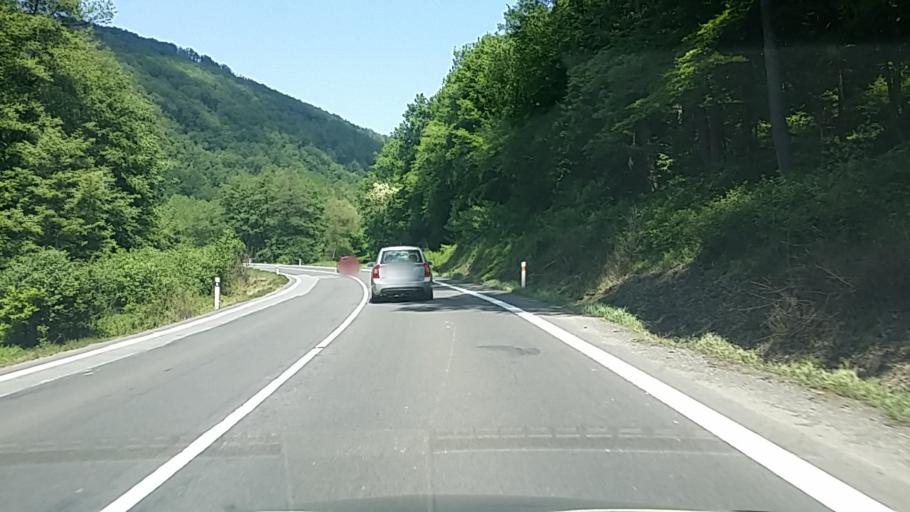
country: SK
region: Banskobystricky
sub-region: Okres Banska Bystrica
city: Zvolen
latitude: 48.5374
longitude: 19.1229
